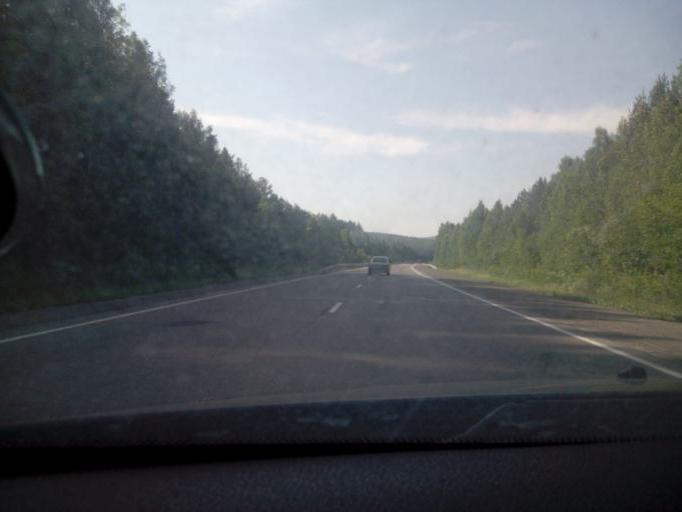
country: RU
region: Sverdlovsk
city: Sredneuralsk
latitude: 57.0723
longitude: 60.4120
